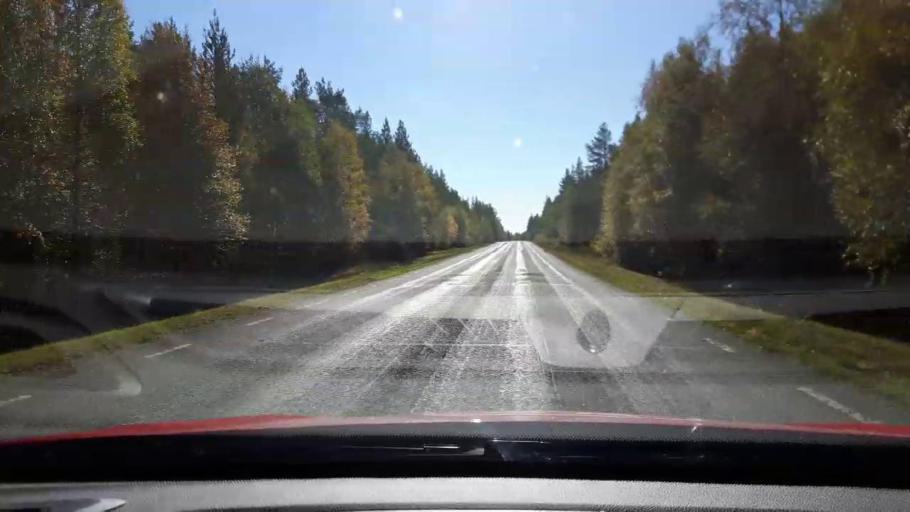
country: SE
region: Jaemtland
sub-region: Harjedalens Kommun
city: Sveg
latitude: 62.3461
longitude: 14.0343
